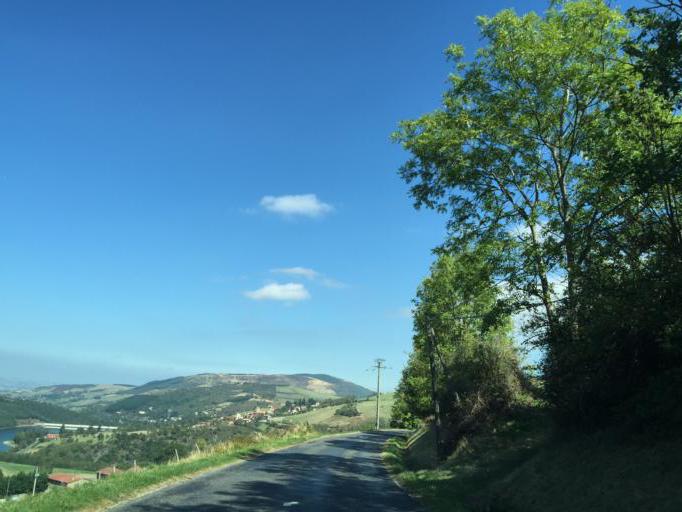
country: FR
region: Rhone-Alpes
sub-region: Departement de la Loire
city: Saint-Paul-en-Jarez
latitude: 45.4282
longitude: 4.5702
